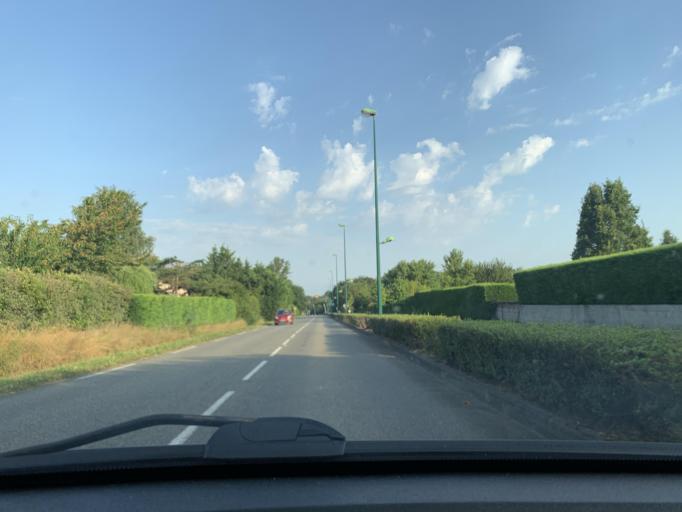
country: FR
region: Midi-Pyrenees
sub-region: Departement de la Haute-Garonne
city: Labege
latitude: 43.5320
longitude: 1.5492
